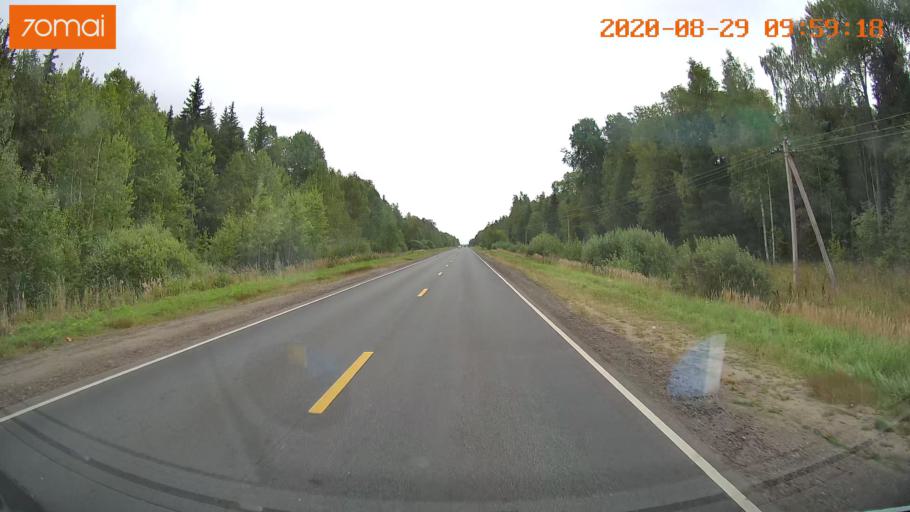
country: RU
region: Ivanovo
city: Zarechnyy
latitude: 57.4113
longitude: 42.3625
